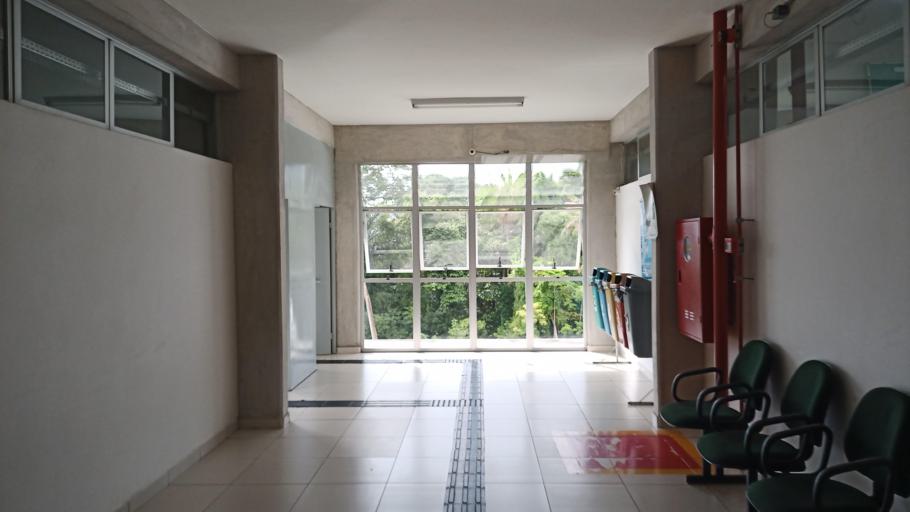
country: BR
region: Amazonas
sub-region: Manaus
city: Manaus
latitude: -3.1010
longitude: -59.9752
